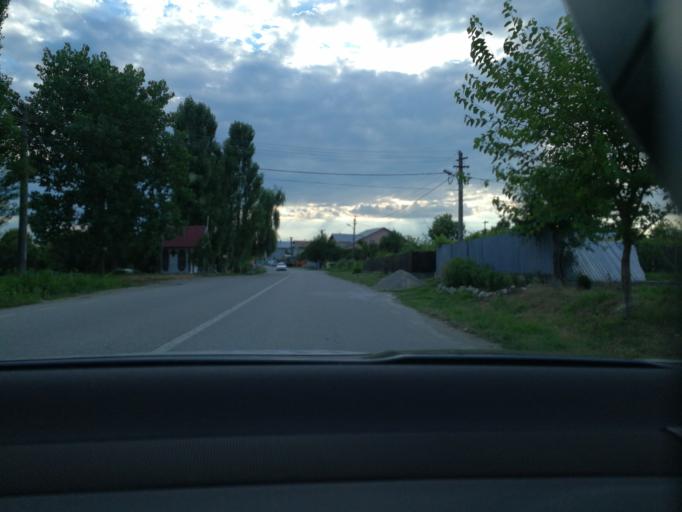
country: RO
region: Prahova
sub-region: Comuna Targsoru Vechi
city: Targsoru Vechi
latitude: 44.8555
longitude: 25.9203
